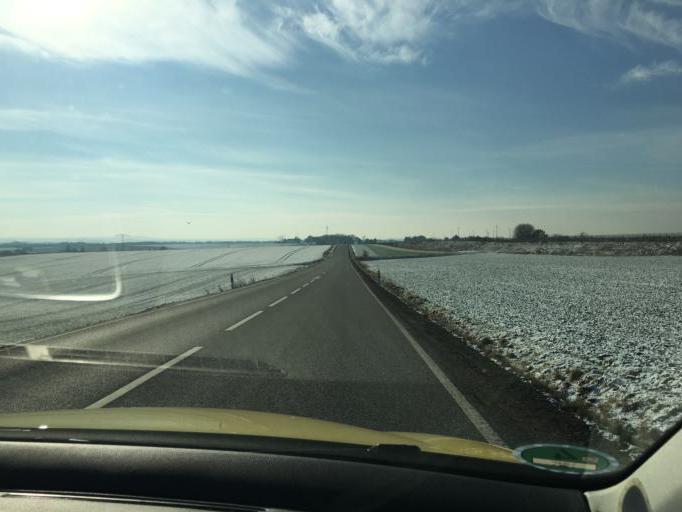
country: DE
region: Saxony
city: Narsdorf
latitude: 50.9805
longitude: 12.6992
